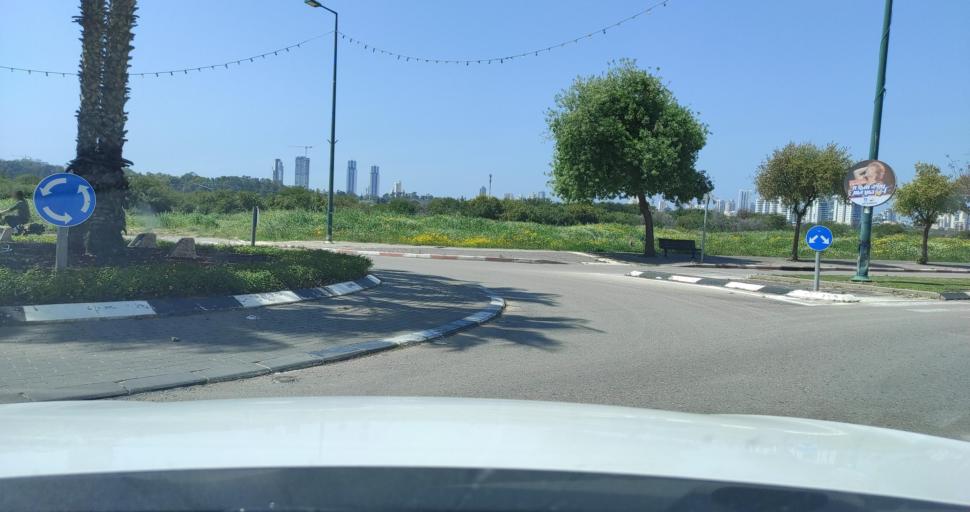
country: IL
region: Central District
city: Nordiyya
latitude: 32.3005
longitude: 34.8696
